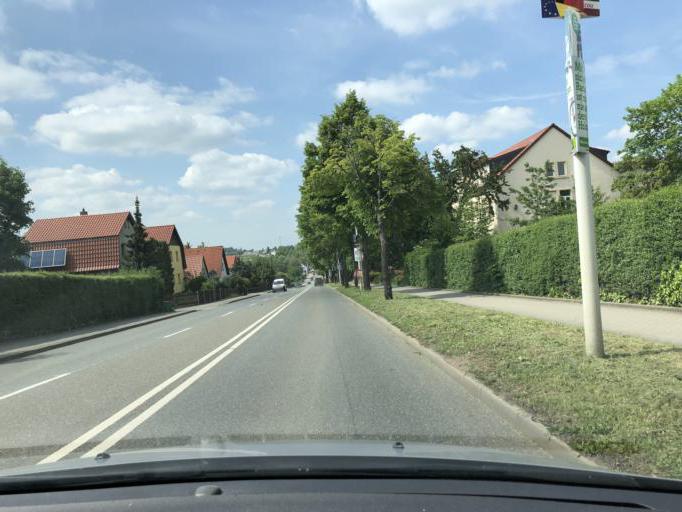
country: DE
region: Thuringia
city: Altenburg
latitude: 50.9902
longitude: 12.4256
